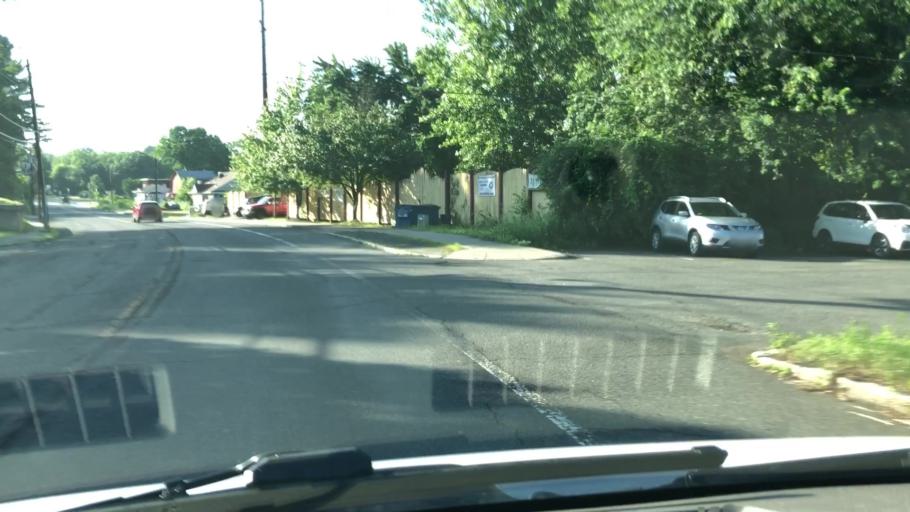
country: US
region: Massachusetts
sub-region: Franklin County
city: Greenfield
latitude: 42.5728
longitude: -72.5959
